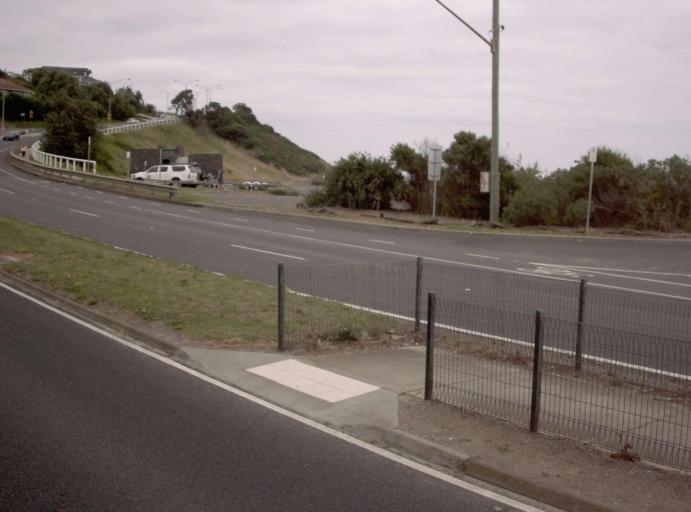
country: AU
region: Victoria
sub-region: Frankston
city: Frankston
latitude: -38.1538
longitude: 145.1102
